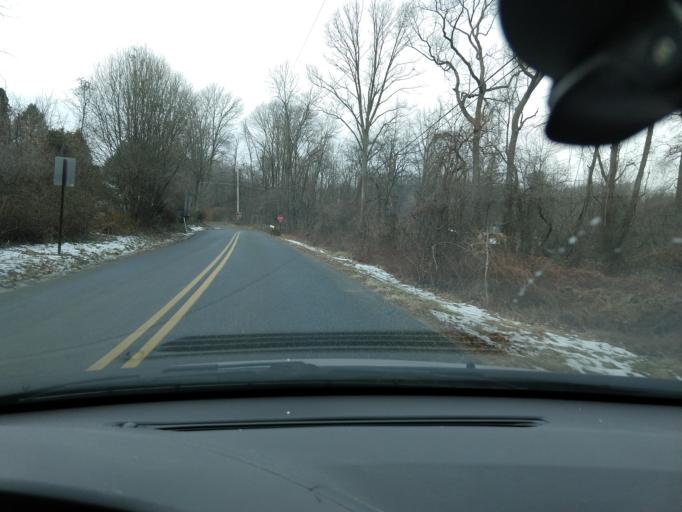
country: US
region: Pennsylvania
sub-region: Berks County
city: Birdsboro
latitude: 40.2438
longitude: -75.7728
